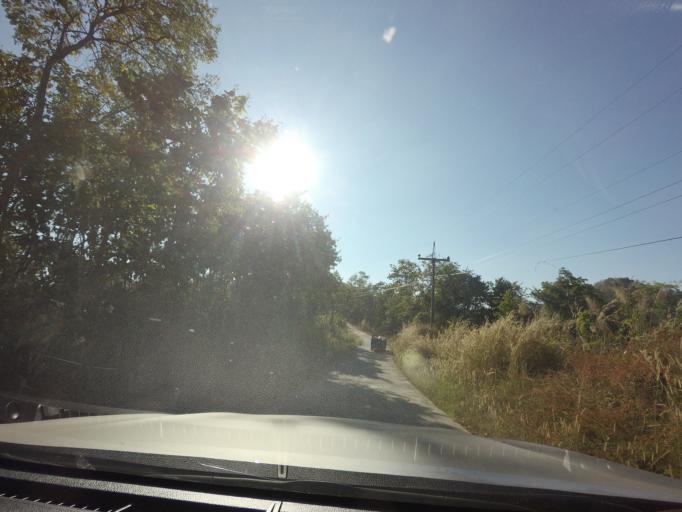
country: TH
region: Lampang
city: Chae Hom
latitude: 18.6152
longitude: 99.6438
